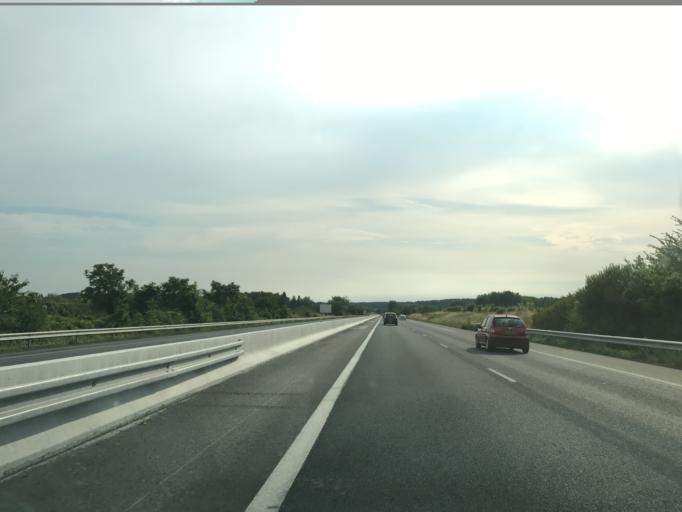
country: FR
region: Poitou-Charentes
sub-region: Departement de la Vienne
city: Naintre
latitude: 46.7657
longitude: 0.4694
